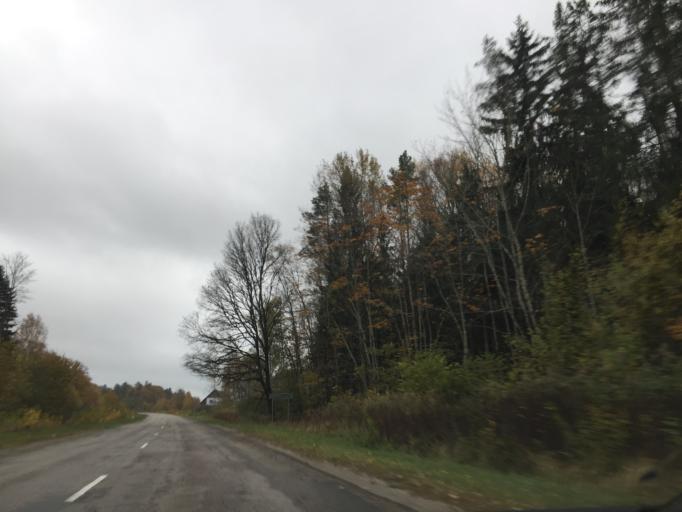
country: LV
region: Pargaujas
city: Stalbe
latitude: 57.3566
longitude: 25.0717
